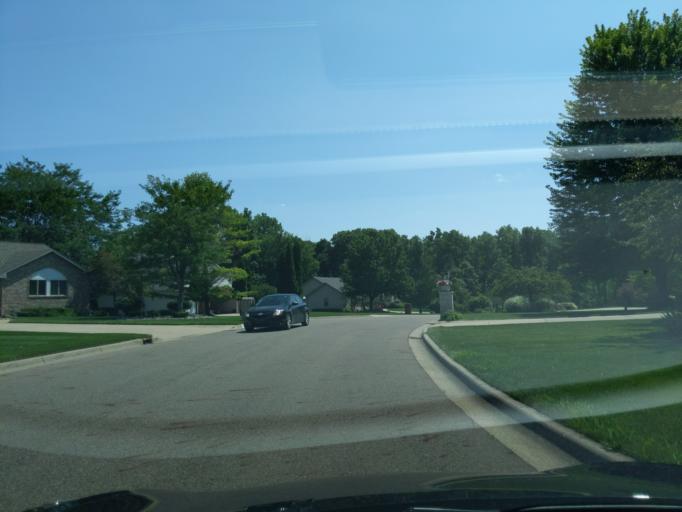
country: US
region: Michigan
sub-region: Ingham County
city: Edgemont Park
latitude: 42.7647
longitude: -84.6111
